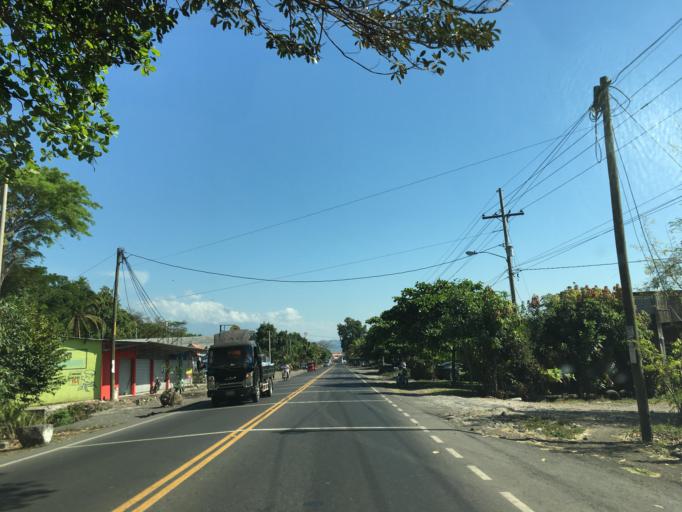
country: GT
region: Escuintla
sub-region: Municipio de La Democracia
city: La Democracia
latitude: 14.2225
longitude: -90.9508
